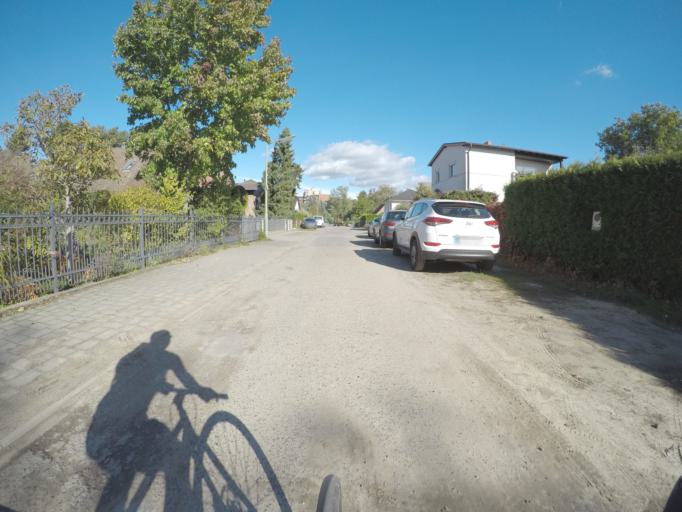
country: DE
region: Berlin
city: Staaken
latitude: 52.5277
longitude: 13.1547
